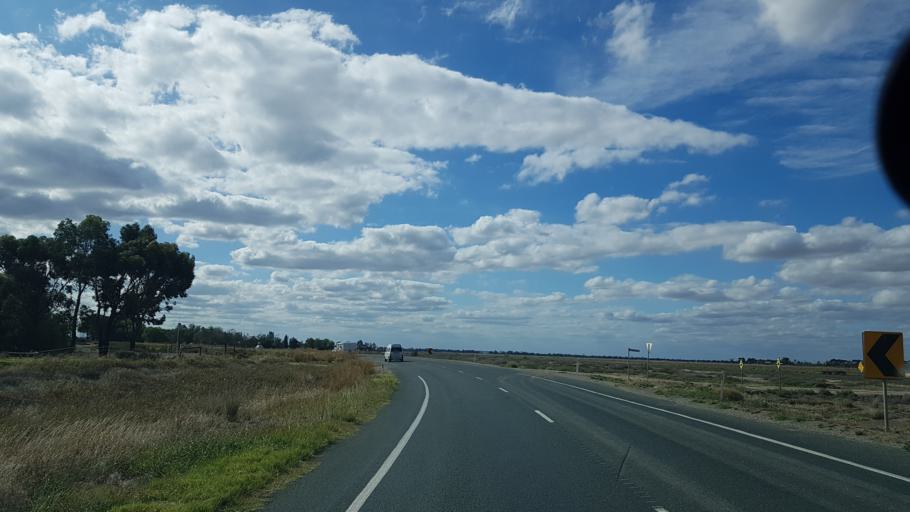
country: AU
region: Victoria
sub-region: Swan Hill
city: Swan Hill
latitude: -35.8008
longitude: 143.9553
